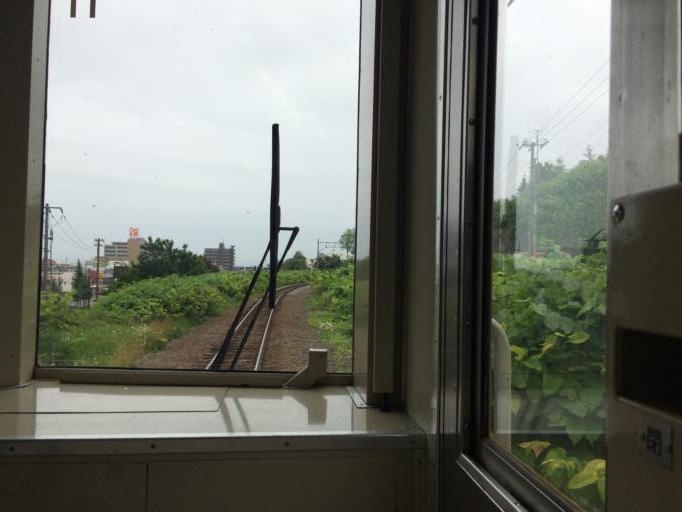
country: JP
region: Hokkaido
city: Otaru
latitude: 43.2017
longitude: 140.9882
